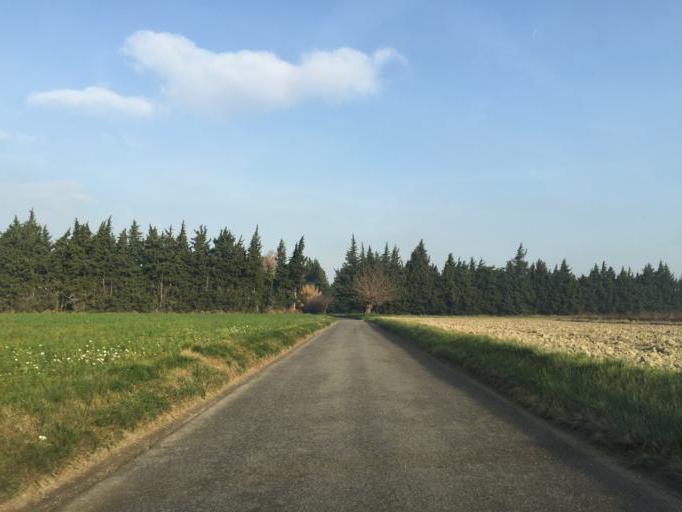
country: FR
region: Provence-Alpes-Cote d'Azur
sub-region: Departement du Vaucluse
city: Courthezon
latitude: 44.0769
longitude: 4.9062
